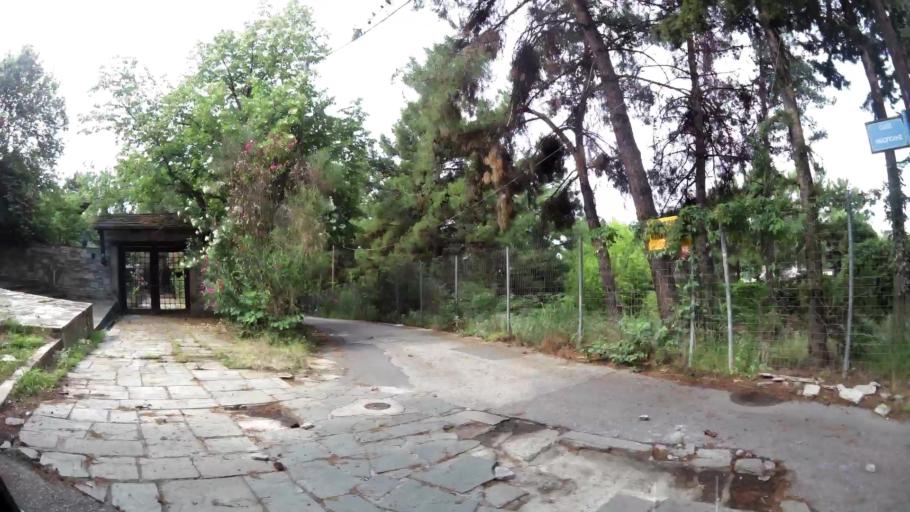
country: GR
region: Central Macedonia
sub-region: Nomos Thessalonikis
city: Panorama
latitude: 40.5900
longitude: 23.0139
